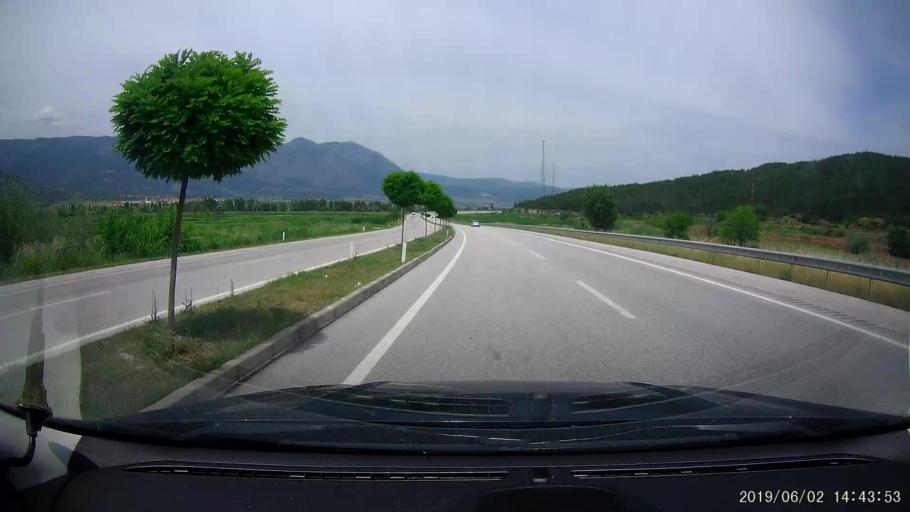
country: TR
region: Corum
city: Hacihamza
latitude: 41.0985
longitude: 34.4003
